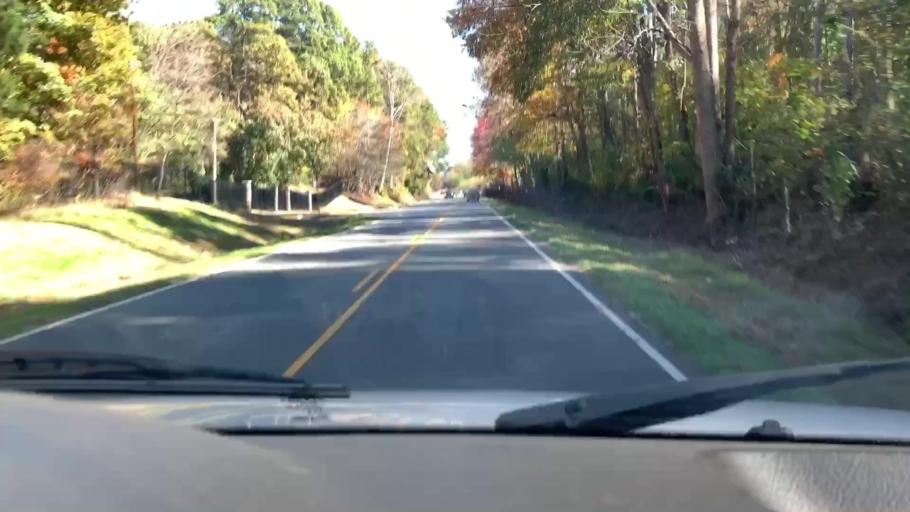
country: US
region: North Carolina
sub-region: Lincoln County
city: Lowesville
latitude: 35.4270
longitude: -80.9511
